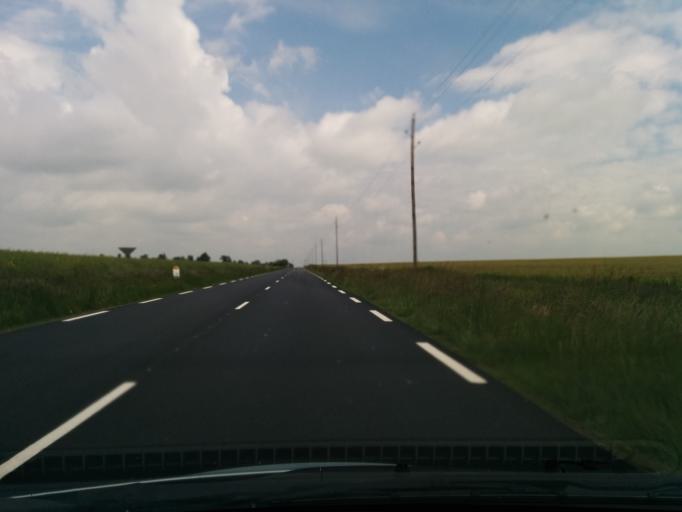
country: FR
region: Ile-de-France
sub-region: Departement des Yvelines
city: Limetz-Villez
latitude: 49.1387
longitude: 1.5272
